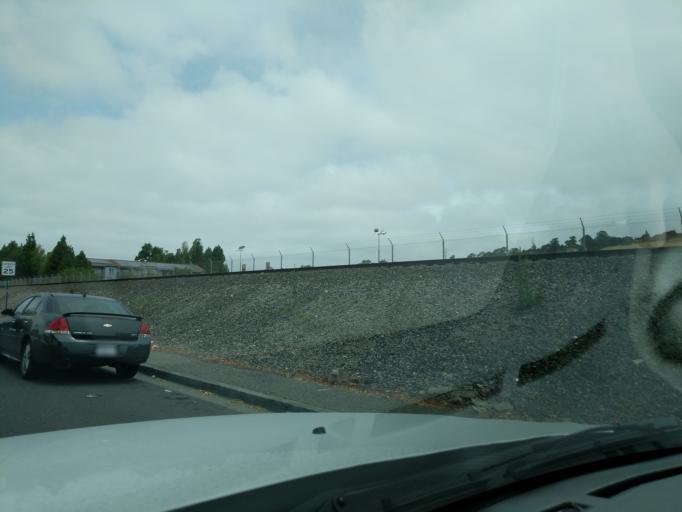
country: US
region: California
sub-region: Alameda County
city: Hayward
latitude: 37.6537
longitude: -122.0729
